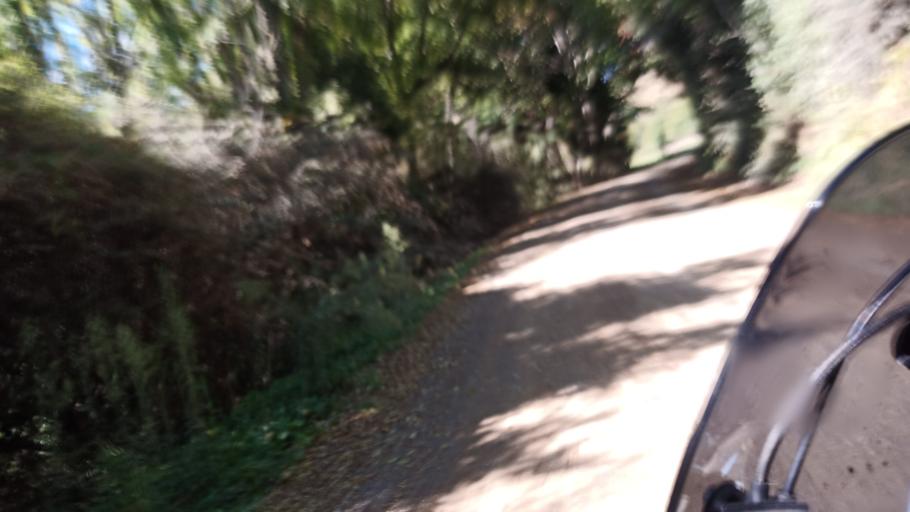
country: NZ
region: Bay of Plenty
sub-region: Opotiki District
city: Opotiki
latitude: -38.2545
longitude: 177.5747
